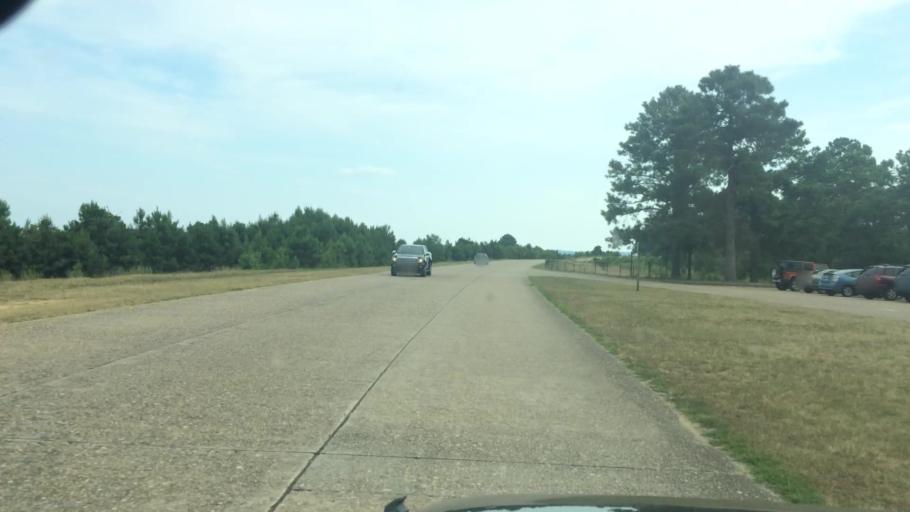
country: US
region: Virginia
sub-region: City of Williamsburg
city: Williamsburg
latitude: 37.2239
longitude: -76.6956
